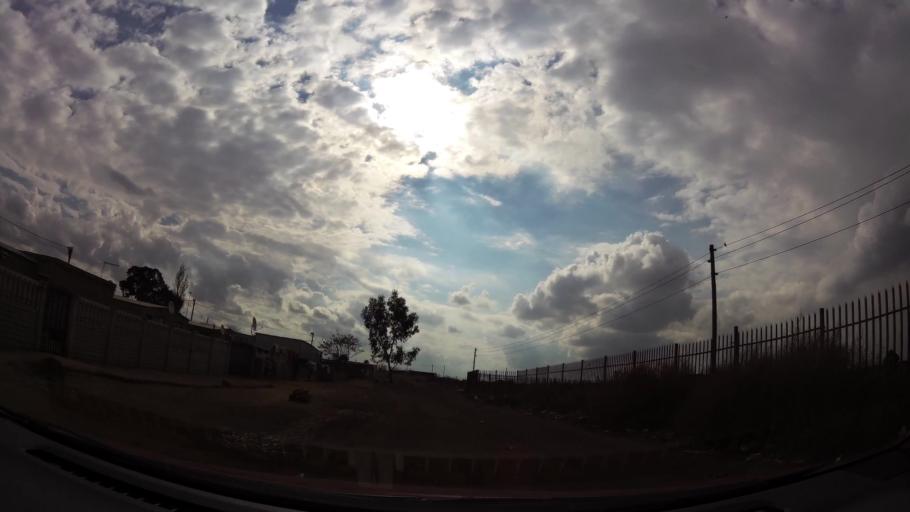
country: ZA
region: Gauteng
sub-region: Sedibeng District Municipality
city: Vanderbijlpark
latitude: -26.6997
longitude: 27.7916
